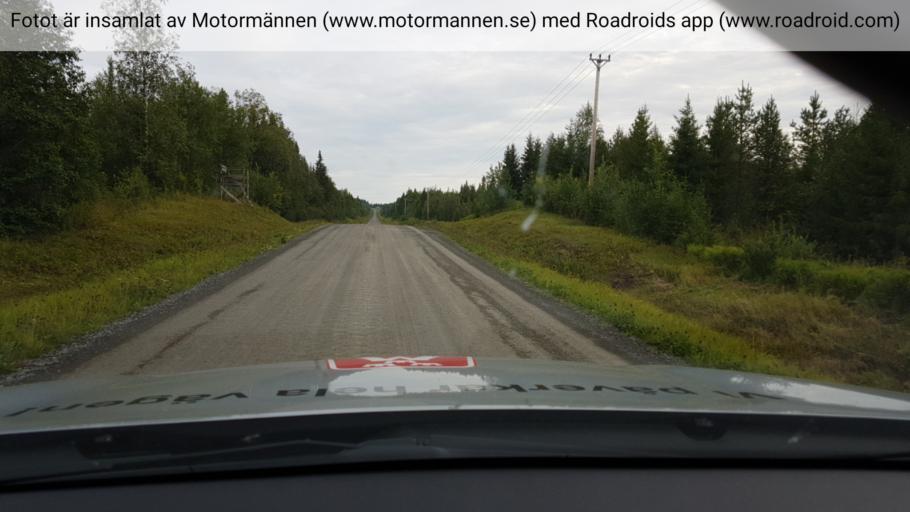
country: SE
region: Jaemtland
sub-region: OEstersunds Kommun
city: Lit
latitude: 63.6284
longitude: 14.9715
